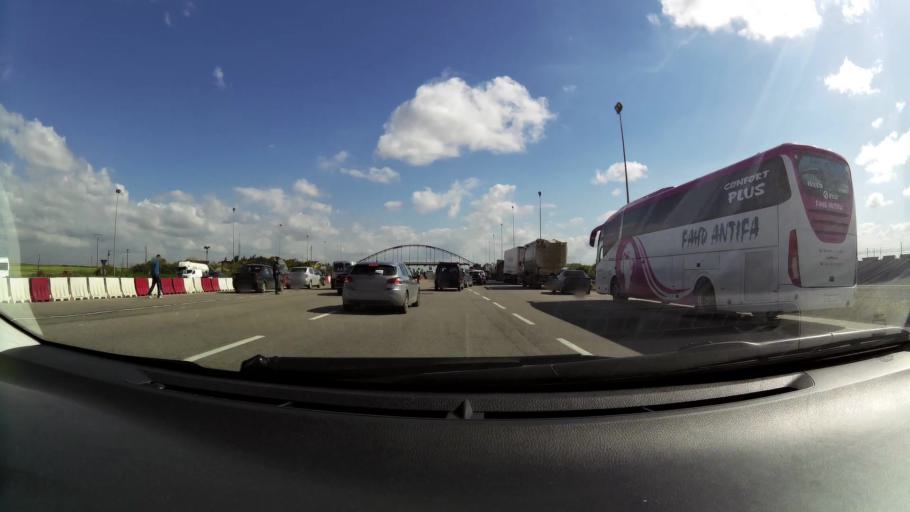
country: MA
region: Chaouia-Ouardigha
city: Nouaseur
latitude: 33.3711
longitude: -7.6211
